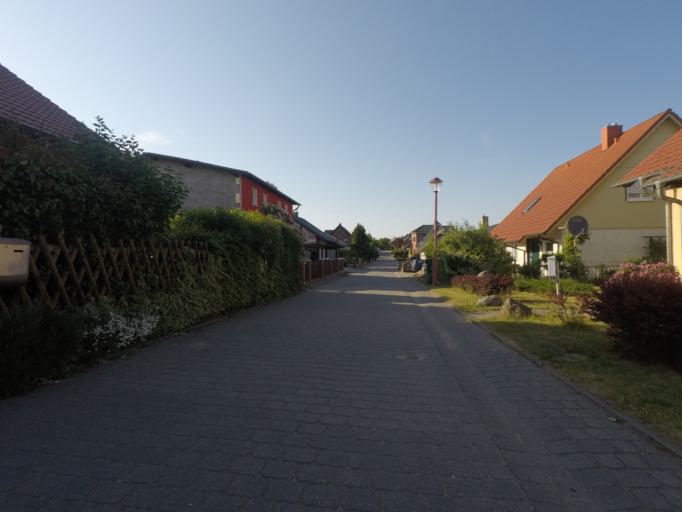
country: DE
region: Brandenburg
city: Joachimsthal
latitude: 52.8924
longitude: 13.7063
